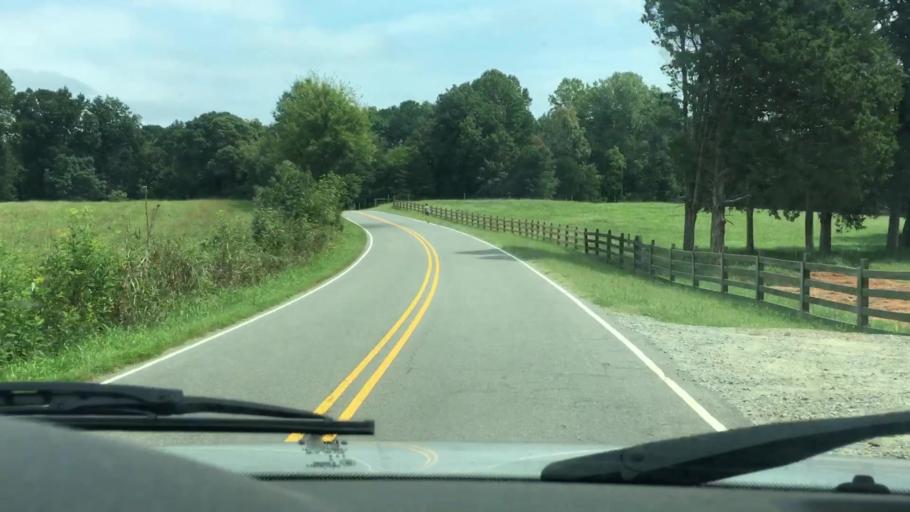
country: US
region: North Carolina
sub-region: Gaston County
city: Davidson
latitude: 35.4987
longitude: -80.8211
